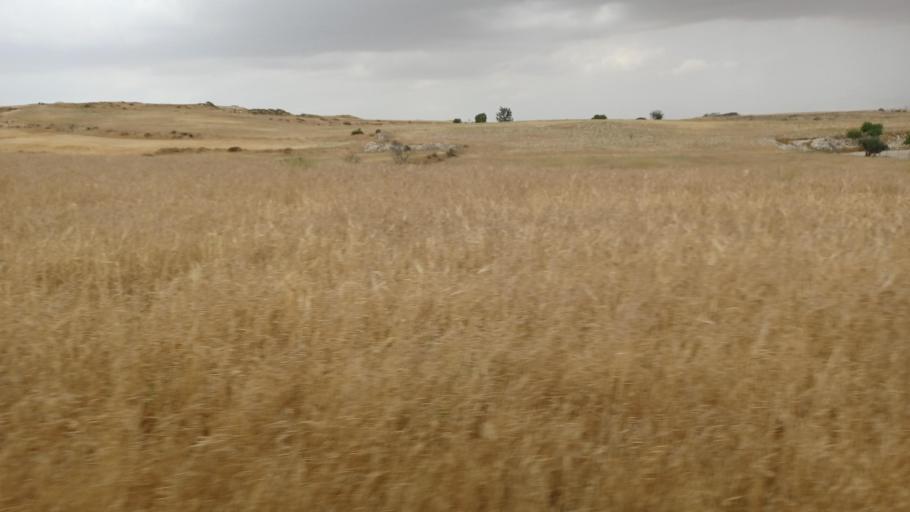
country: CY
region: Larnaka
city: Athienou
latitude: 35.0334
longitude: 33.5704
